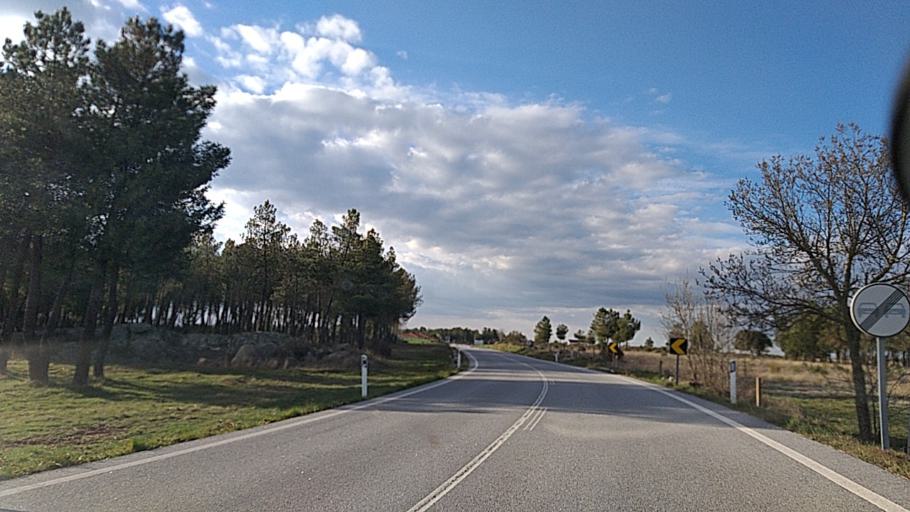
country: ES
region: Castille and Leon
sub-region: Provincia de Salamanca
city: Aldea del Obispo
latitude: 40.6701
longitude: -6.8596
